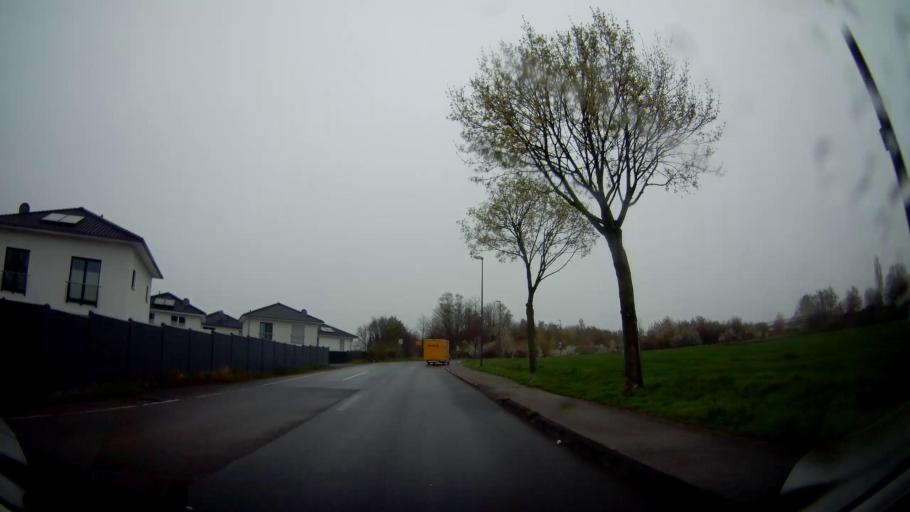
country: DE
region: North Rhine-Westphalia
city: Castrop-Rauxel
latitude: 51.5311
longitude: 7.3254
